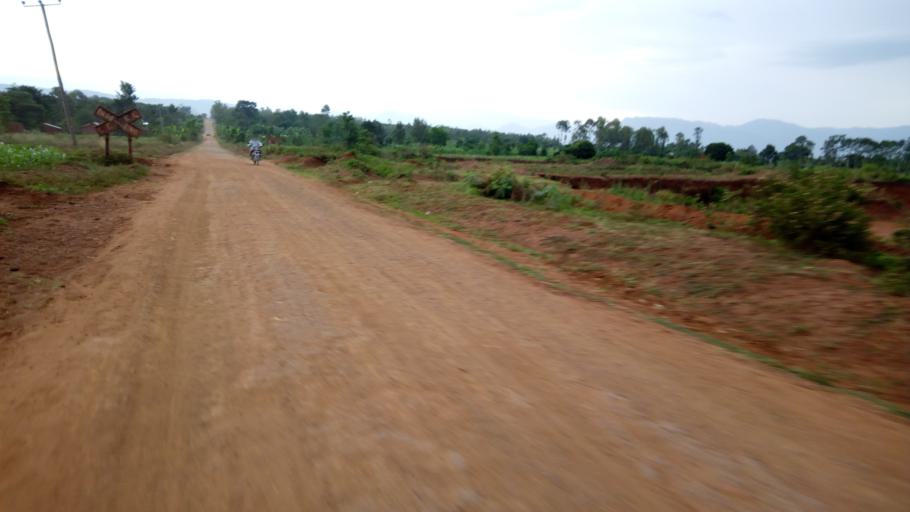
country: UG
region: Eastern Region
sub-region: Mbale District
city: Mbale
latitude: 1.1415
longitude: 34.1346
